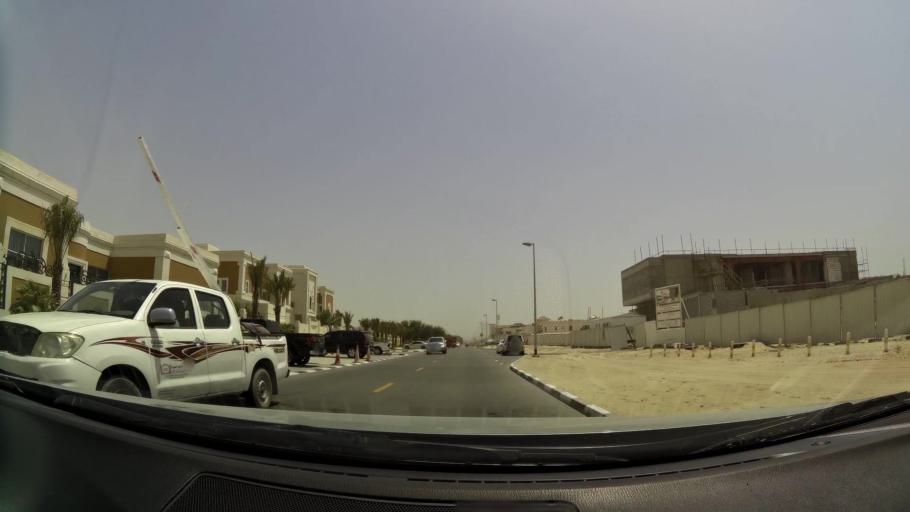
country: AE
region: Dubai
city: Dubai
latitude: 25.1361
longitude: 55.2086
